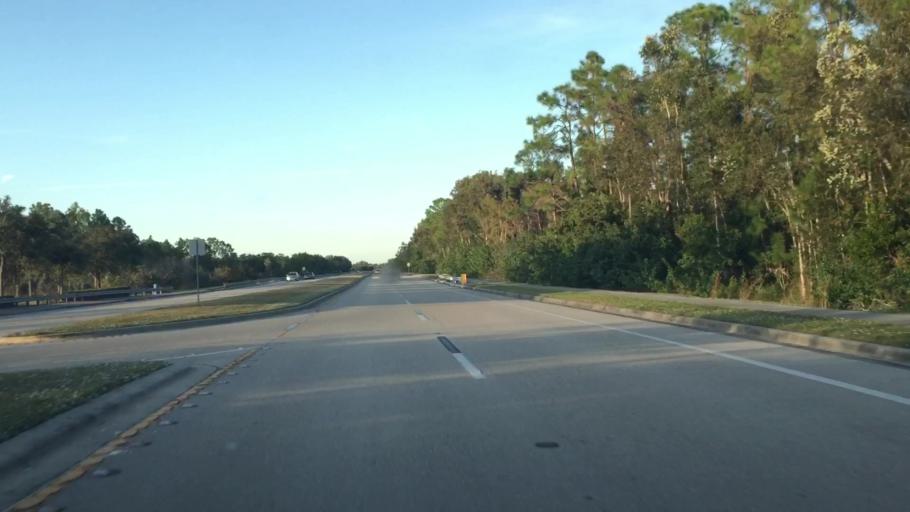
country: US
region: Florida
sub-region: Lee County
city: Estero
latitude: 26.4077
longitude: -81.8046
